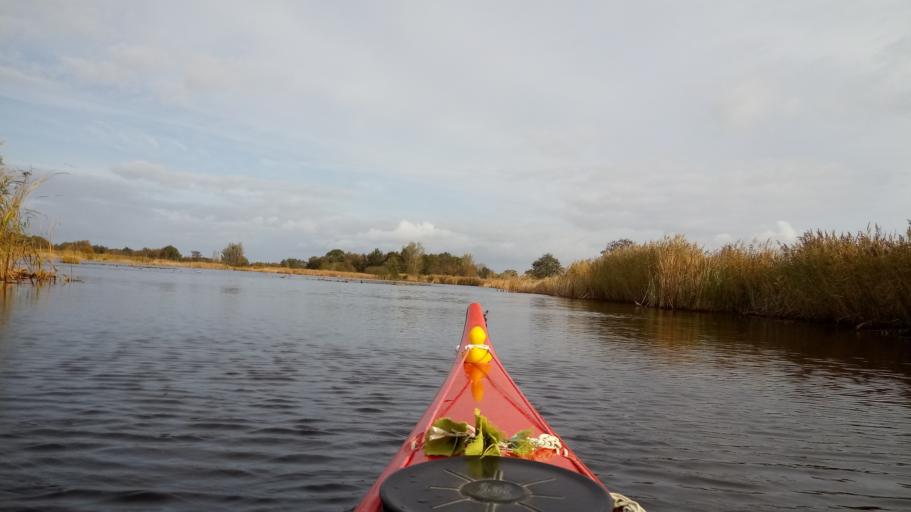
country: NL
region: Overijssel
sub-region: Gemeente Steenwijkerland
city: Sint Jansklooster
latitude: 52.6657
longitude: 6.0449
